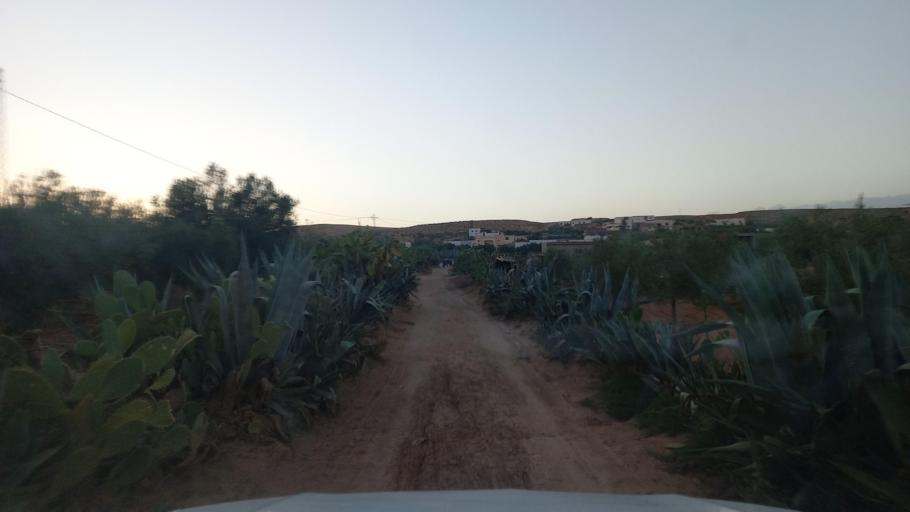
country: TN
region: Al Qasrayn
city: Sbiba
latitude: 35.3767
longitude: 9.0165
